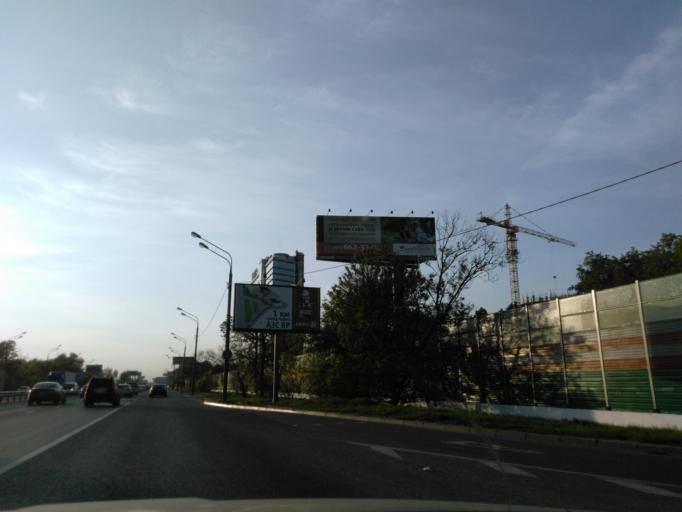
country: RU
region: Moscow
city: Khimki
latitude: 55.8919
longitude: 37.4324
